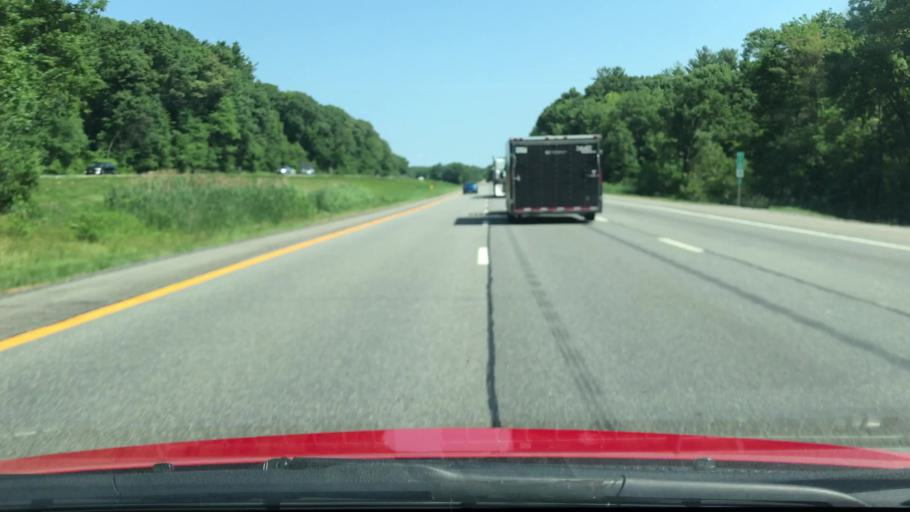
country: US
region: New York
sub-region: Albany County
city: Cohoes
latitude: 42.8285
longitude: -73.7694
